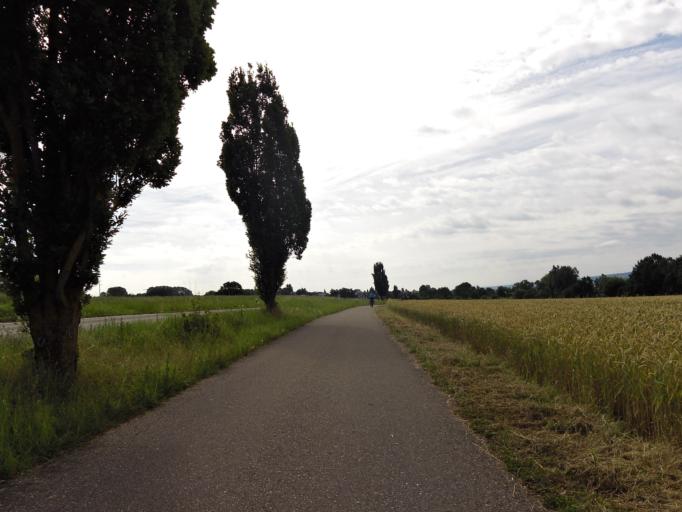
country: DE
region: Baden-Wuerttemberg
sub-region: Freiburg Region
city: Allensbach
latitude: 47.7244
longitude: 9.0448
